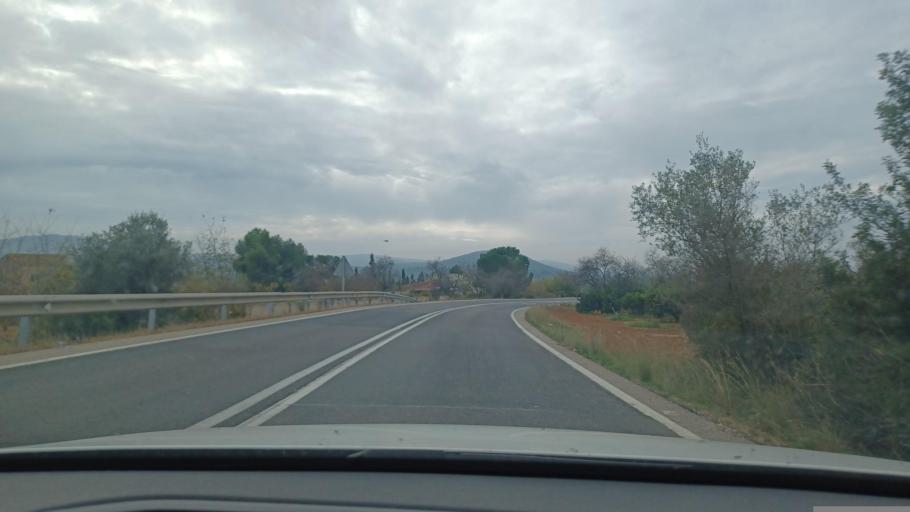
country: ES
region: Catalonia
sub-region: Provincia de Tarragona
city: Santa Barbara
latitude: 40.6800
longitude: 0.4587
